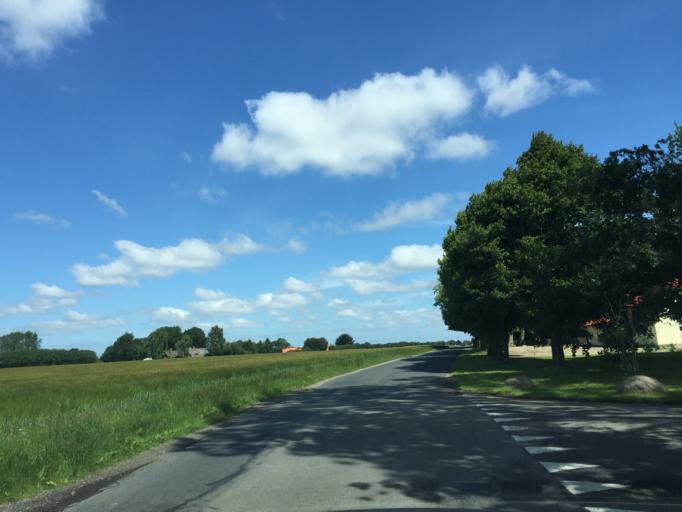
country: DK
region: South Denmark
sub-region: Odense Kommune
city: Hojby
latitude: 55.3175
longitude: 10.4272
